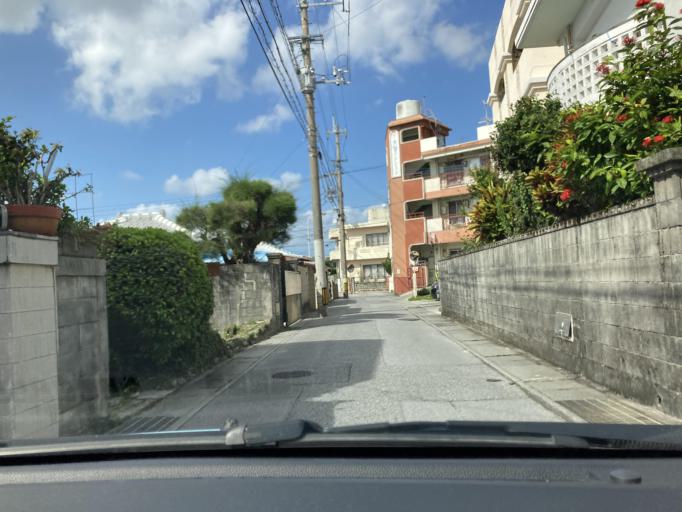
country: JP
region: Okinawa
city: Naha-shi
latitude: 26.2116
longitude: 127.7127
